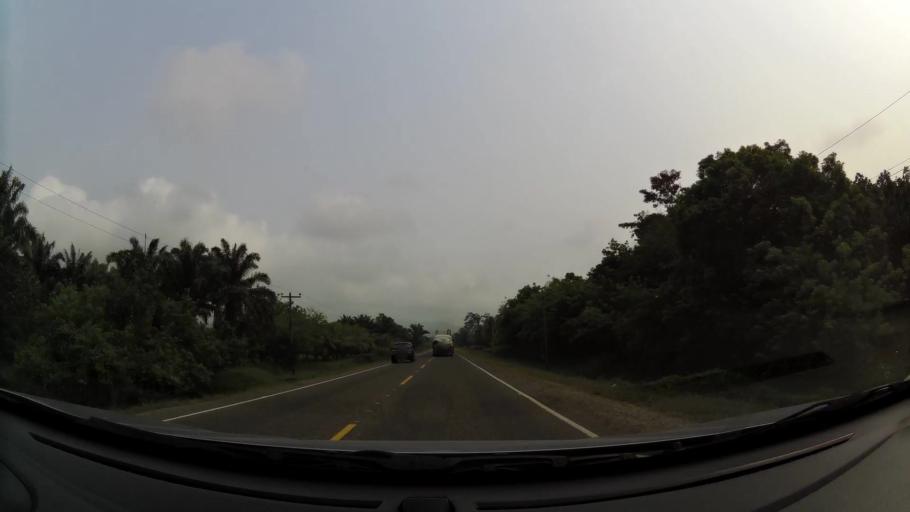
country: HN
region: Atlantida
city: Mezapa
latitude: 15.6166
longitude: -87.6153
